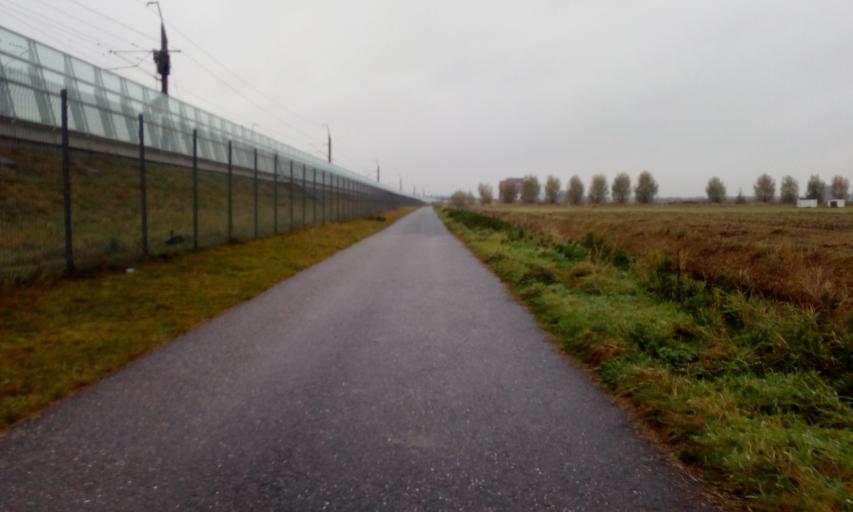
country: NL
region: South Holland
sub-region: Gemeente Lansingerland
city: Berkel en Rodenrijs
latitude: 51.9805
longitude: 4.4731
